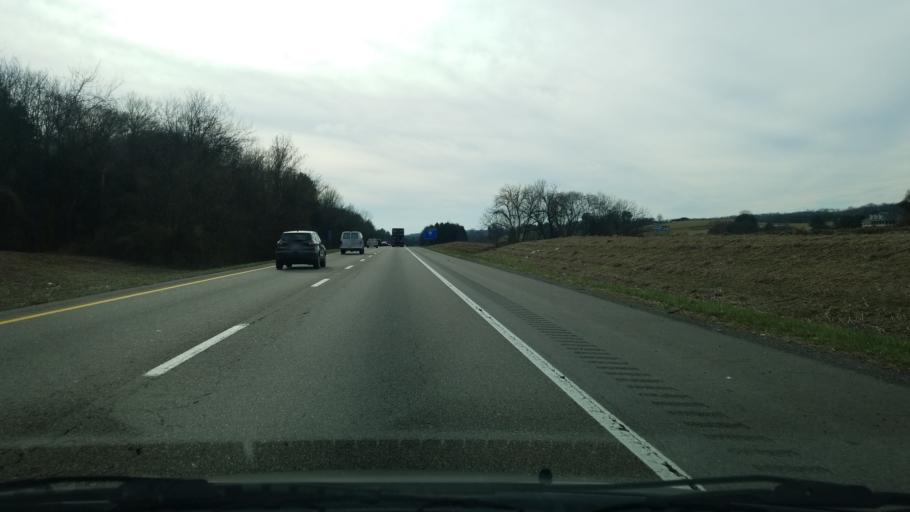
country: US
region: Tennessee
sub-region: Loudon County
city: Lenoir City
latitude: 35.7976
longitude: -84.3207
